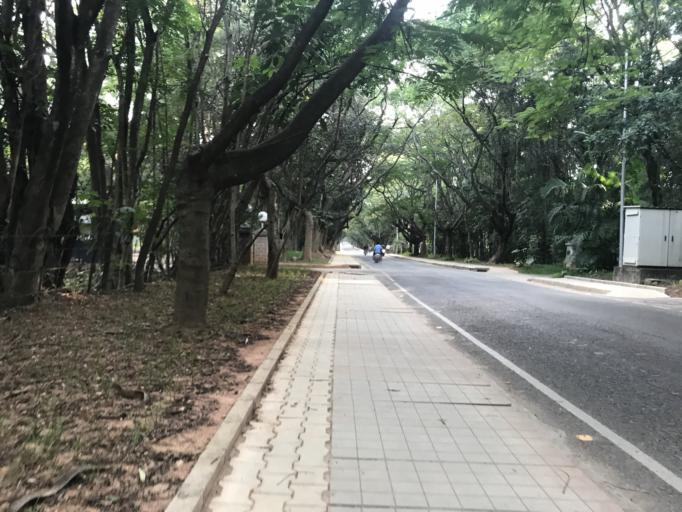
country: IN
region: Karnataka
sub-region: Bangalore Urban
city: Bangalore
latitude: 13.0214
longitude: 77.5665
